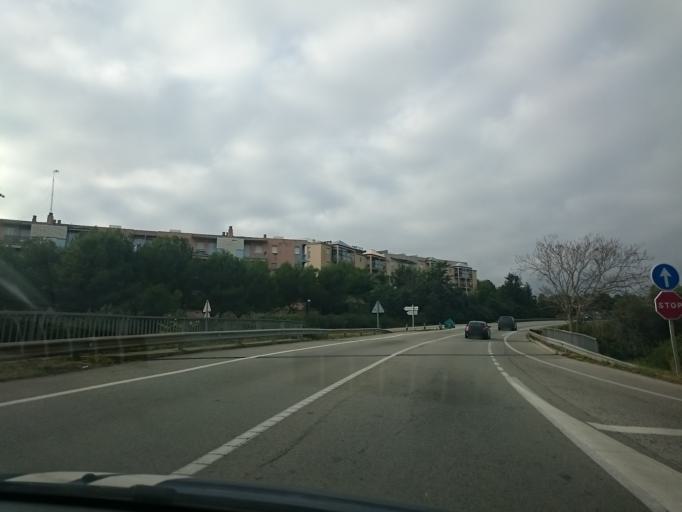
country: ES
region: Catalonia
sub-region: Provincia de Barcelona
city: Sitges
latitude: 41.2399
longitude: 1.8195
